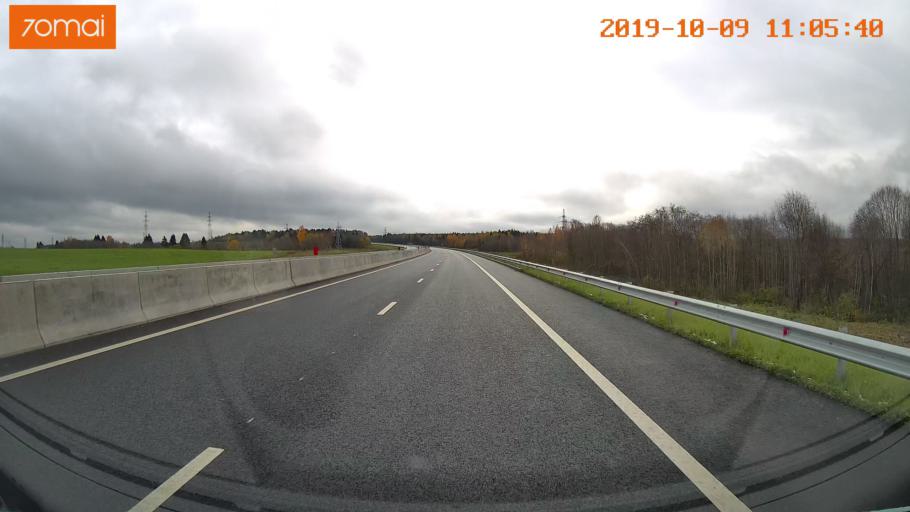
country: RU
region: Vologda
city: Molochnoye
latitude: 59.1968
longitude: 39.7580
